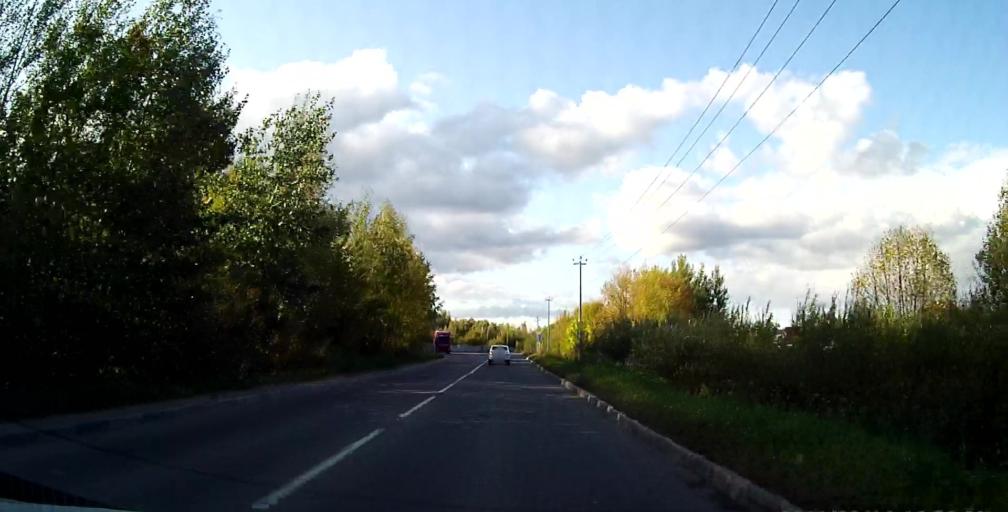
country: RU
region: Moskovskaya
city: Klimovsk
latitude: 55.3748
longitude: 37.5640
